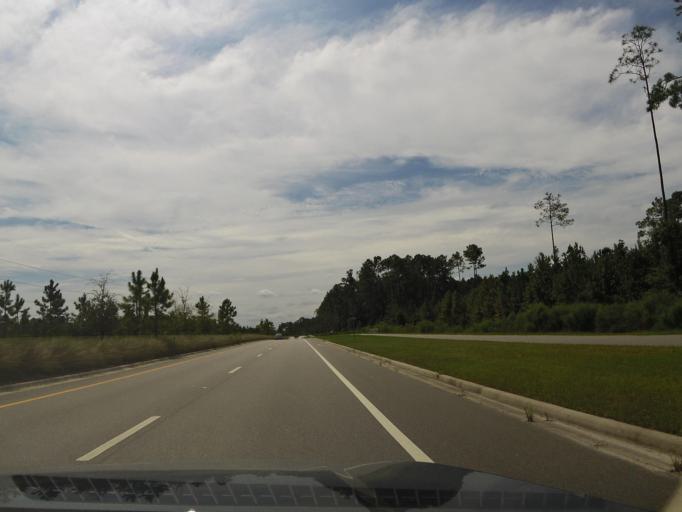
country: US
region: Florida
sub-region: Saint Johns County
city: Fruit Cove
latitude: 30.0458
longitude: -81.5297
